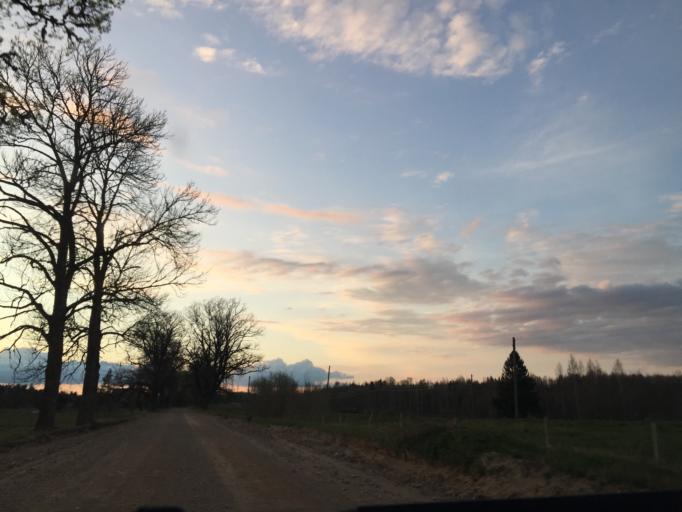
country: LV
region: Aluksnes Rajons
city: Aluksne
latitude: 57.2809
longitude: 26.9183
